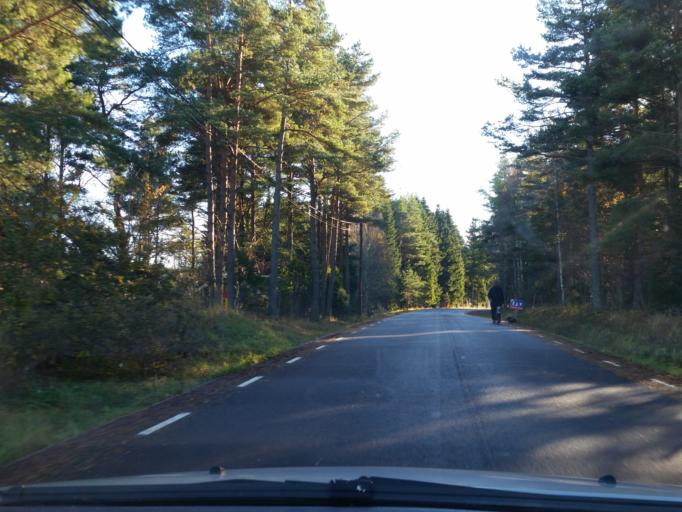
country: AX
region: Alands landsbygd
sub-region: Jomala
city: Jomala
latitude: 60.2001
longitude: 19.9576
